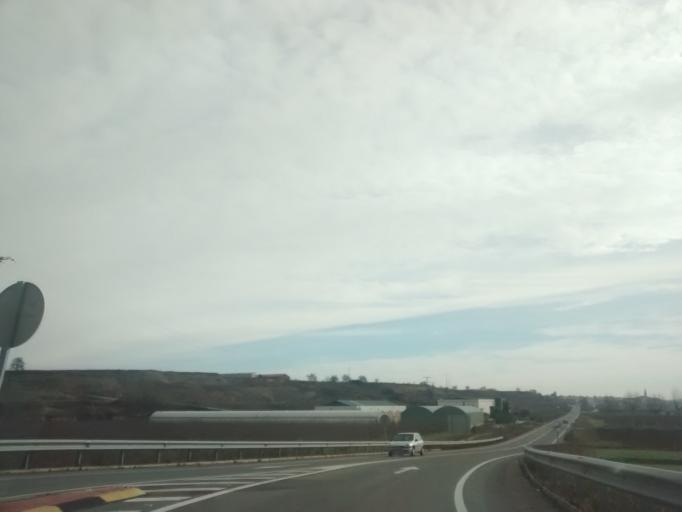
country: ES
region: Navarre
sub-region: Provincia de Navarra
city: Mendavia
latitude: 42.4520
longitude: -2.2282
